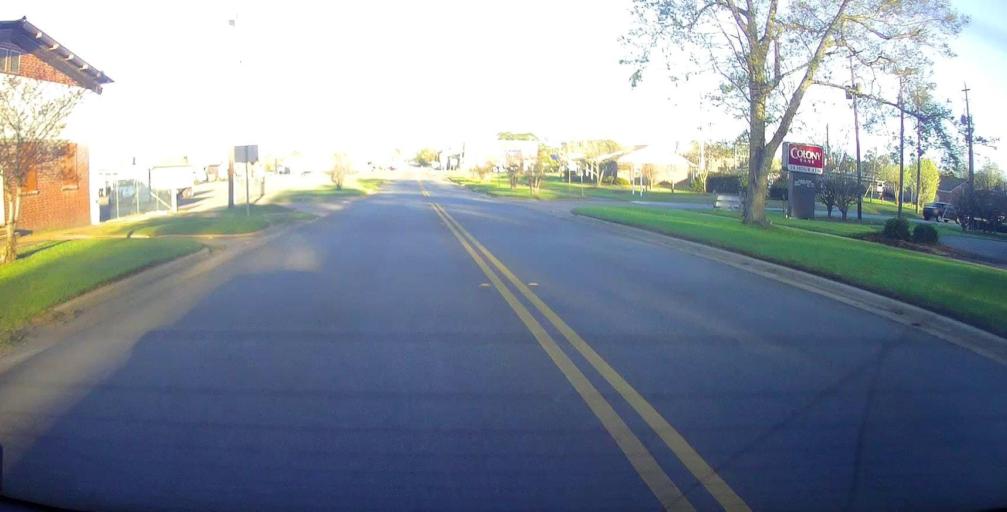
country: US
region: Georgia
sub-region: Wilcox County
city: Rochelle
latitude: 31.9509
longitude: -83.4583
